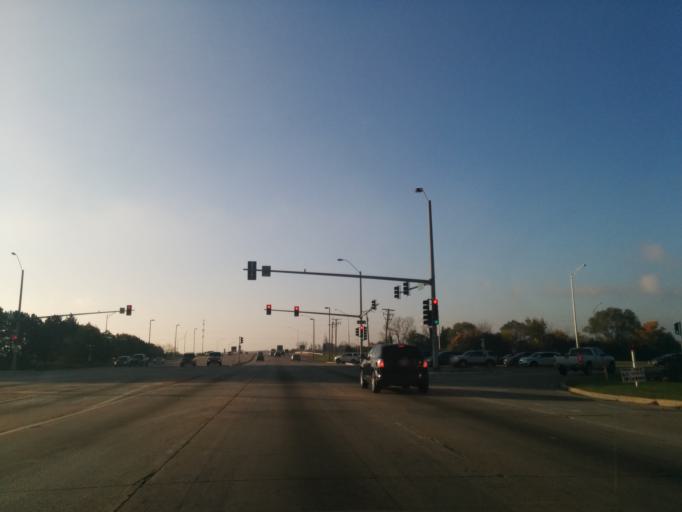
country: US
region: Illinois
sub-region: DuPage County
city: Oakbrook Terrace
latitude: 41.8473
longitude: -87.9579
